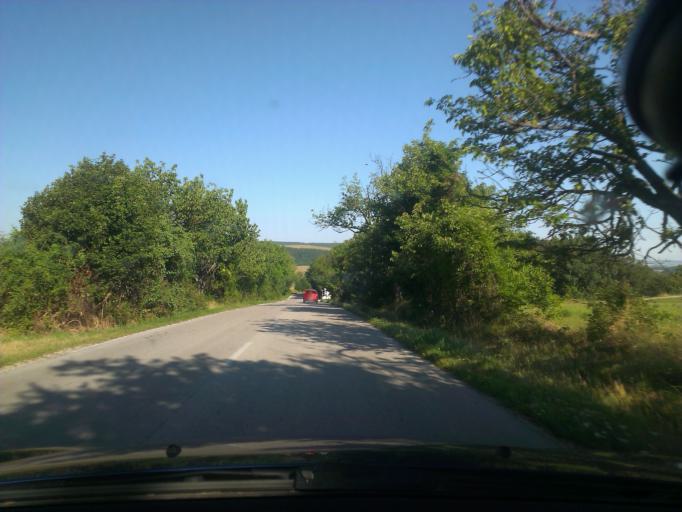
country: SK
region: Trnavsky
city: Vrbove
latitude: 48.6827
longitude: 17.6847
